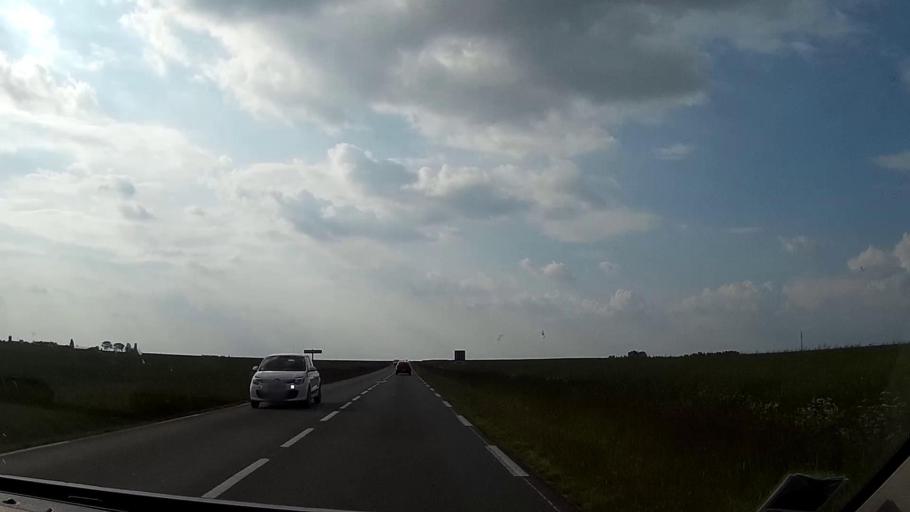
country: FR
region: Centre
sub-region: Departement du Loir-et-Cher
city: Herbault
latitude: 47.7036
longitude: 1.1741
